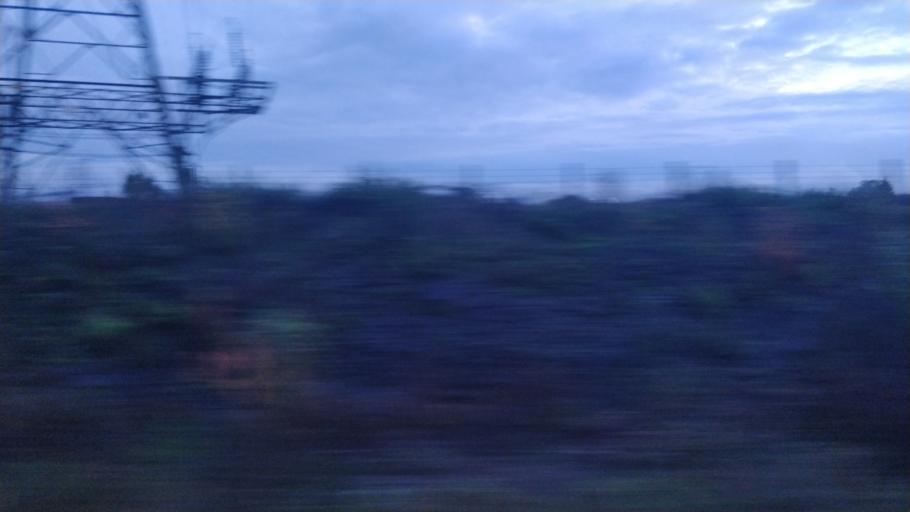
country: GB
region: England
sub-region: Borough of Bolton
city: Westhoughton
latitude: 53.5387
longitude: -2.5117
